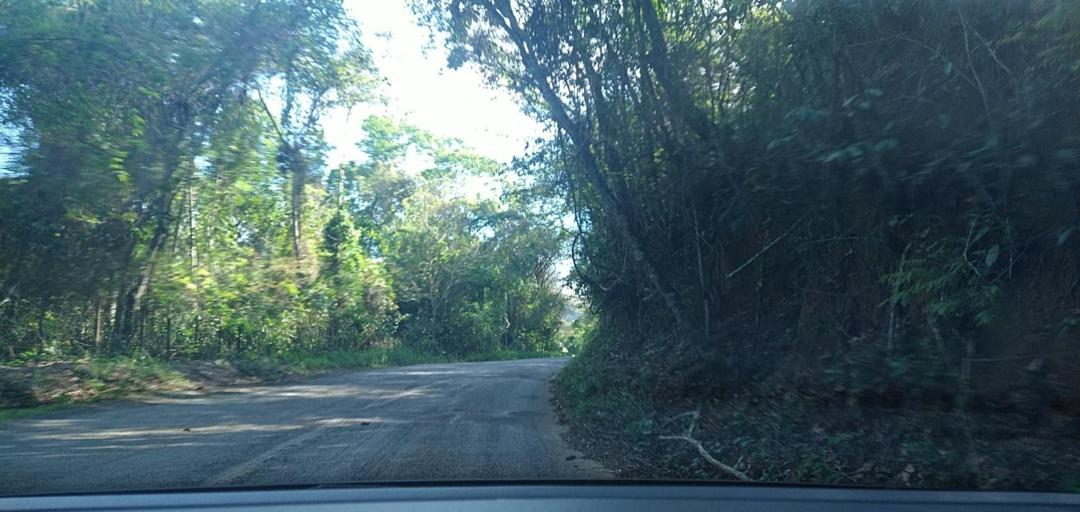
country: BR
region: Minas Gerais
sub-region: Alvinopolis
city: Alvinopolis
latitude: -20.1726
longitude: -42.9216
